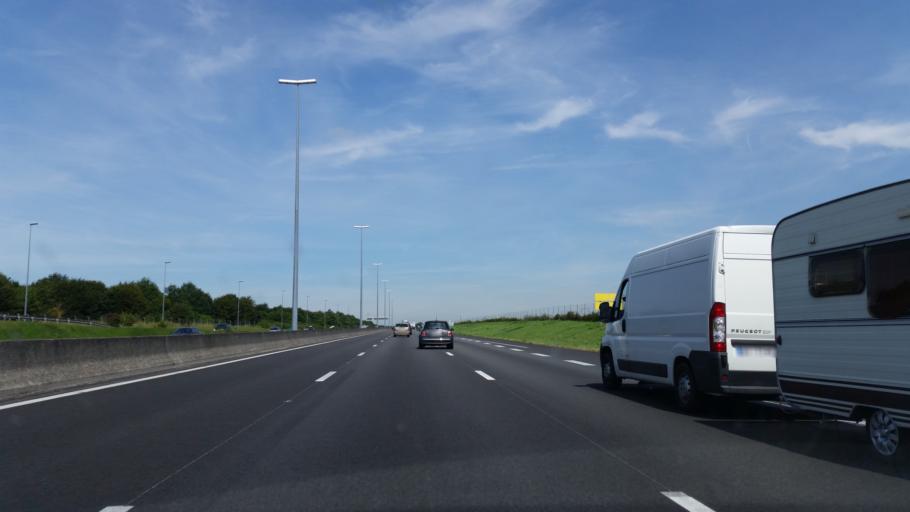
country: FR
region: Picardie
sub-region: Departement de la Somme
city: Chaulnes
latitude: 49.8543
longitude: 2.8329
